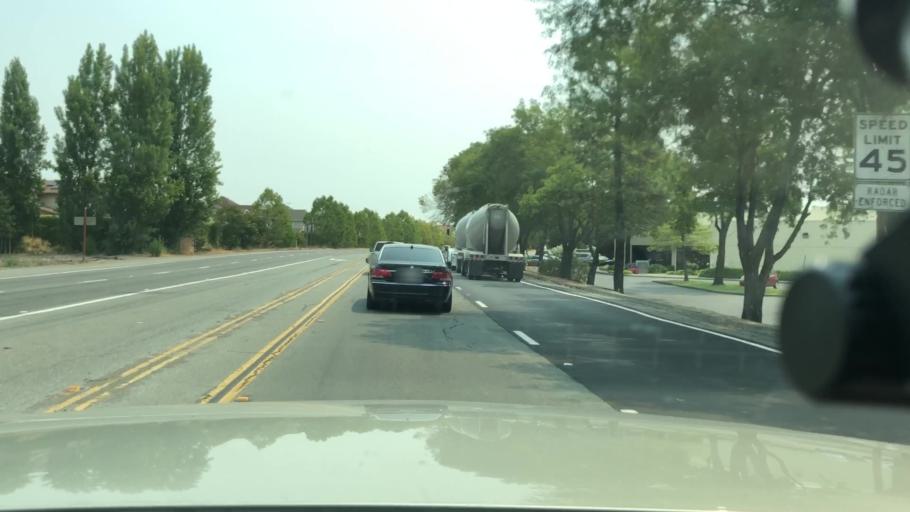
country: US
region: California
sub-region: Sonoma County
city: Petaluma
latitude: 38.2346
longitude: -122.5934
